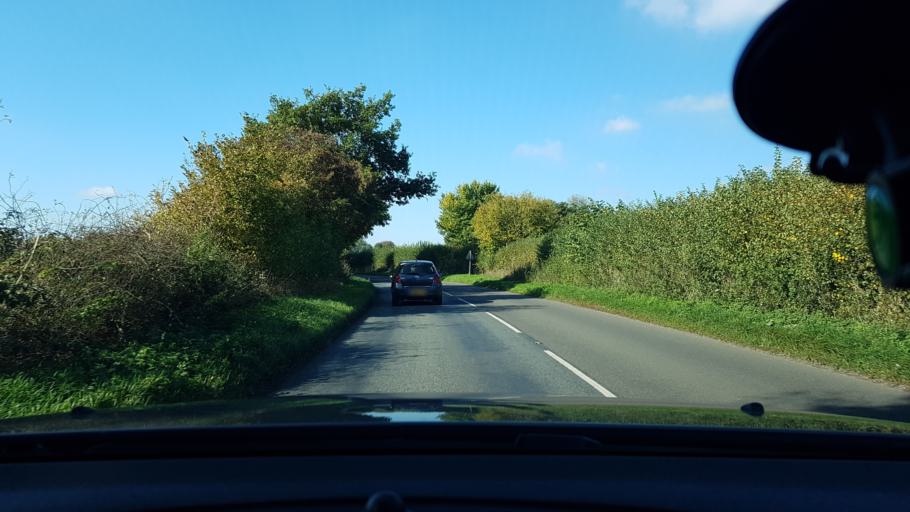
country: GB
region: England
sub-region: Wiltshire
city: Chilton Foliat
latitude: 51.4354
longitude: -1.5578
